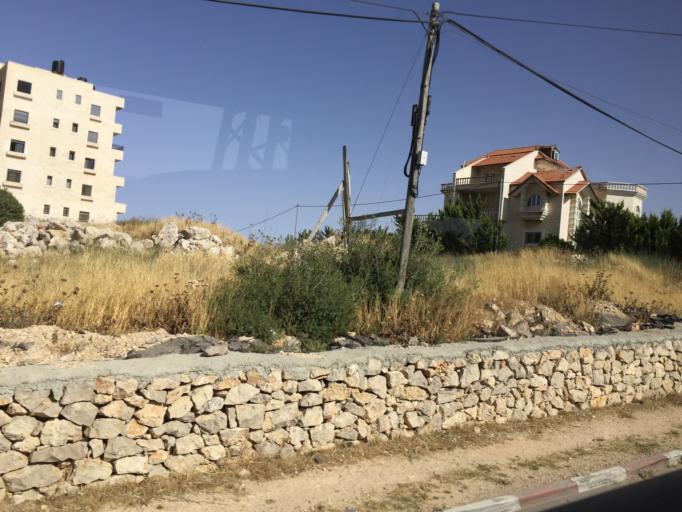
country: PS
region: West Bank
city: Bayt Jala
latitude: 31.7133
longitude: 35.1751
